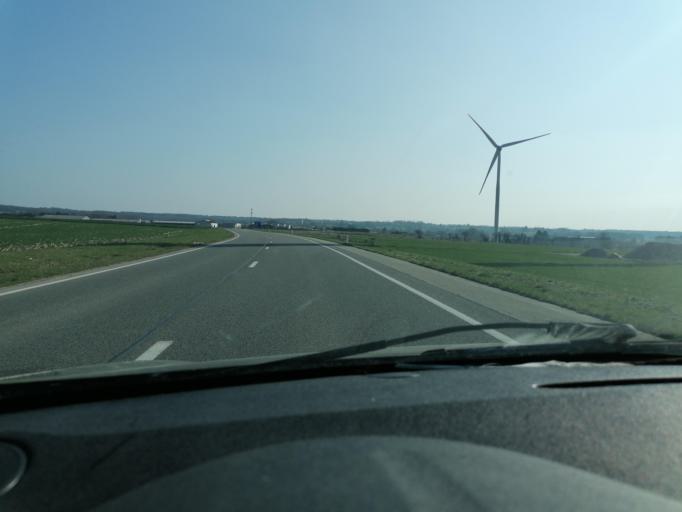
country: BE
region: Wallonia
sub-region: Province du Hainaut
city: Chimay
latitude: 50.0440
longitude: 4.3778
